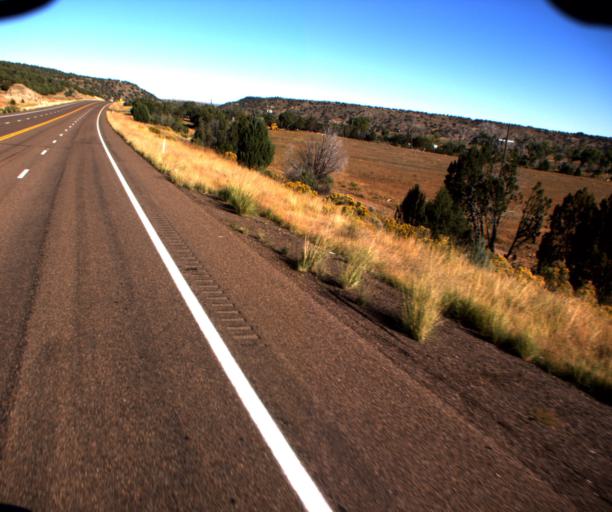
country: US
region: Arizona
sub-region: Navajo County
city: White Mountain Lake
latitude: 34.3785
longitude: -110.0560
